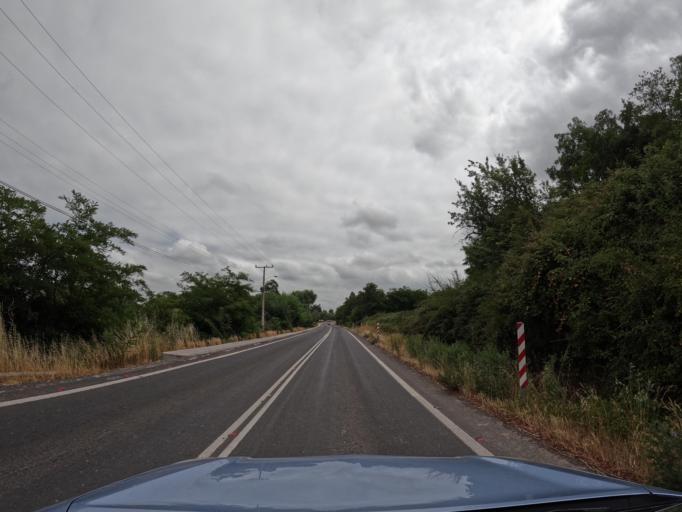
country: CL
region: Maule
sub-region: Provincia de Curico
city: Teno
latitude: -34.7915
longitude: -71.2284
